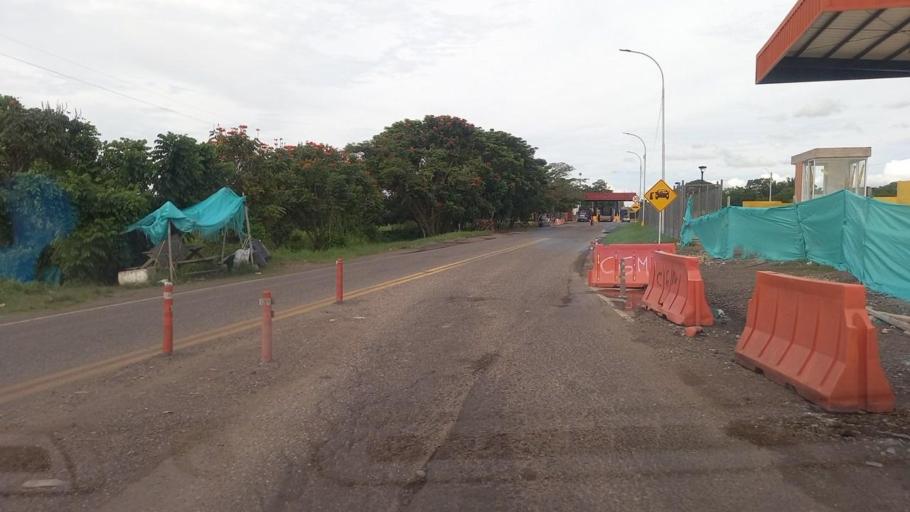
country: CO
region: Antioquia
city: Puerto Berrio
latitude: 6.2934
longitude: -74.4580
